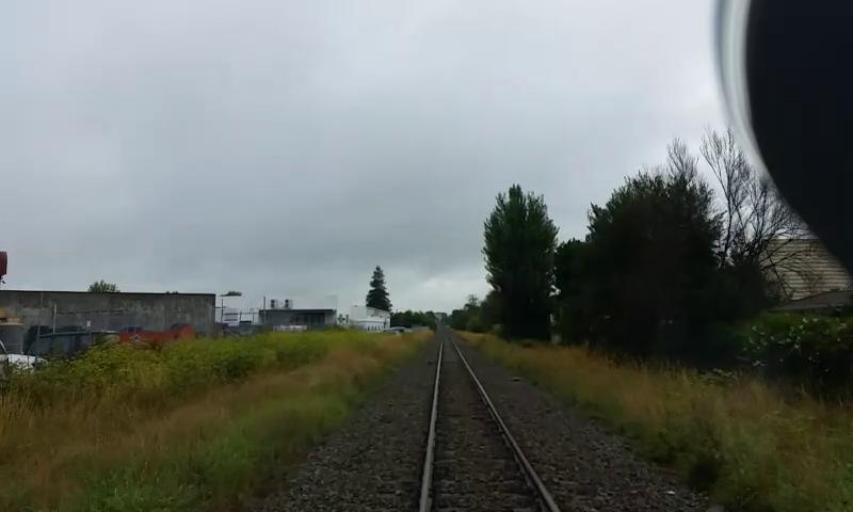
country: NZ
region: Canterbury
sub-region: Christchurch City
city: Christchurch
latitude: -43.5332
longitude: 172.6092
